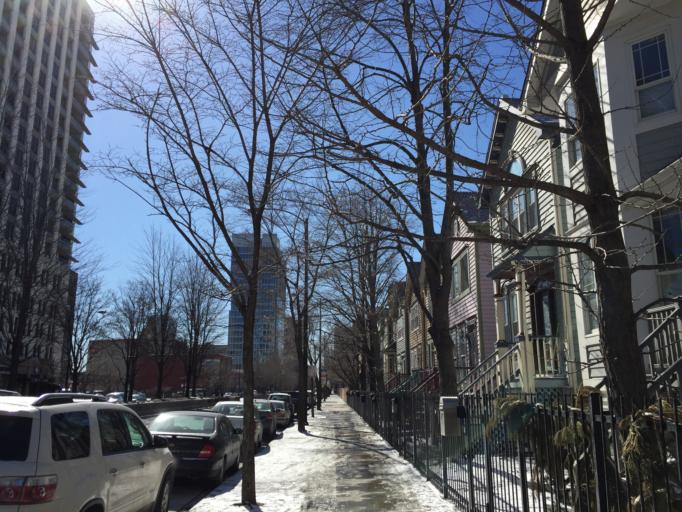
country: US
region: Illinois
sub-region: Cook County
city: Chicago
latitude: 41.8667
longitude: -87.6276
